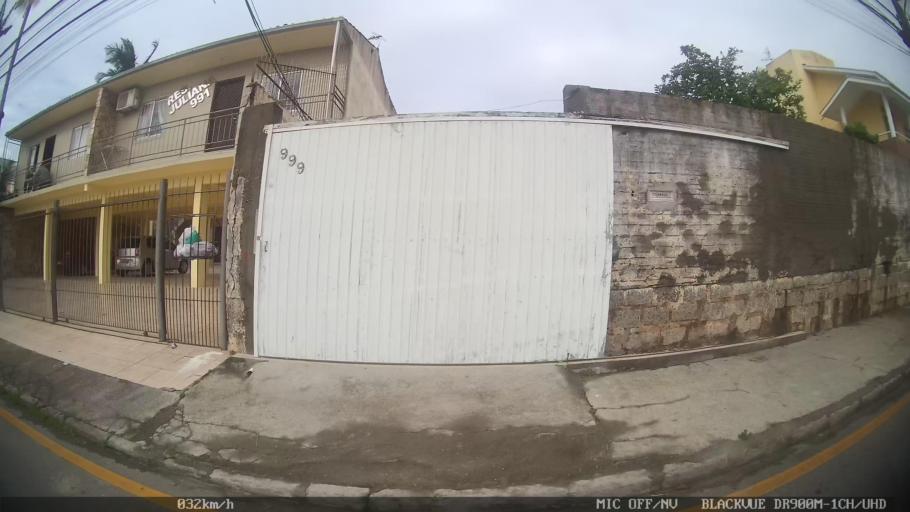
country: BR
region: Santa Catarina
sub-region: Sao Jose
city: Campinas
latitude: -27.5697
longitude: -48.6206
